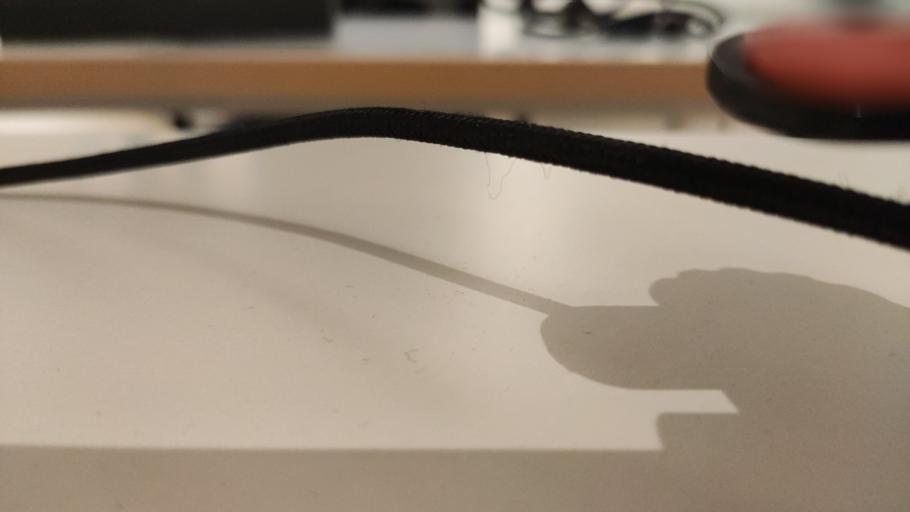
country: RU
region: Moskovskaya
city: Dorokhovo
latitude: 55.3907
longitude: 36.3915
